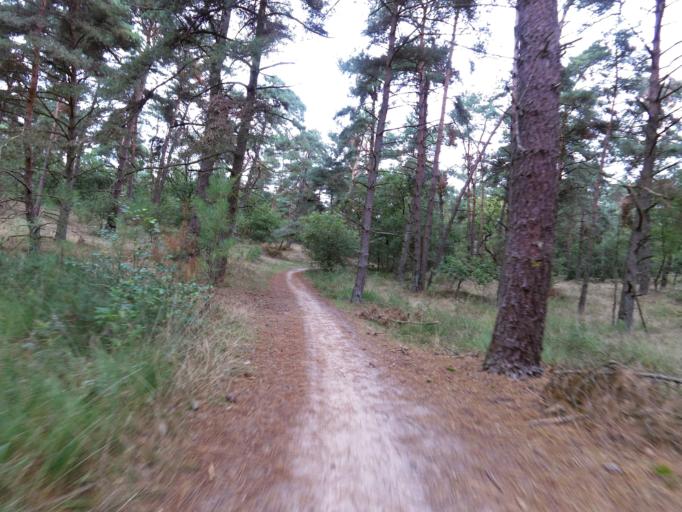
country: NL
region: North Brabant
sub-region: Gemeente Loon op Zand
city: Loon op Zand
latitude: 51.6522
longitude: 5.1322
